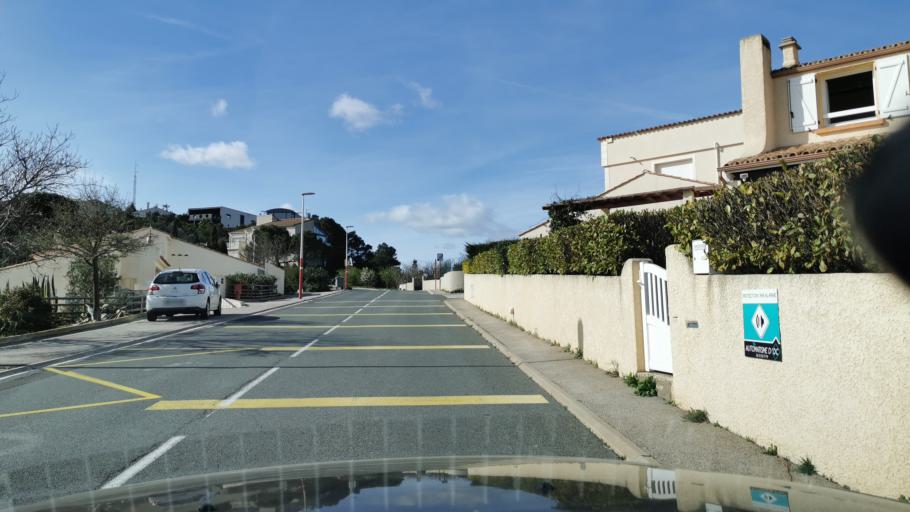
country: FR
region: Languedoc-Roussillon
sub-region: Departement de l'Aude
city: Narbonne
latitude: 43.1645
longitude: 2.9762
